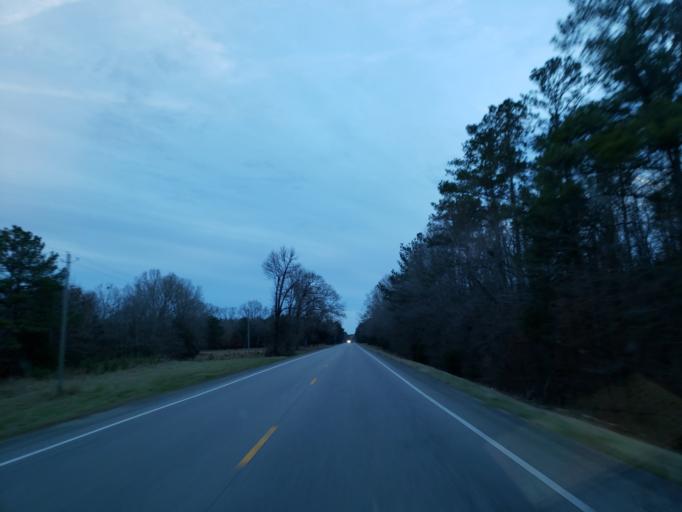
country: US
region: Alabama
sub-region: Sumter County
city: Livingston
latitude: 32.8198
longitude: -88.3106
